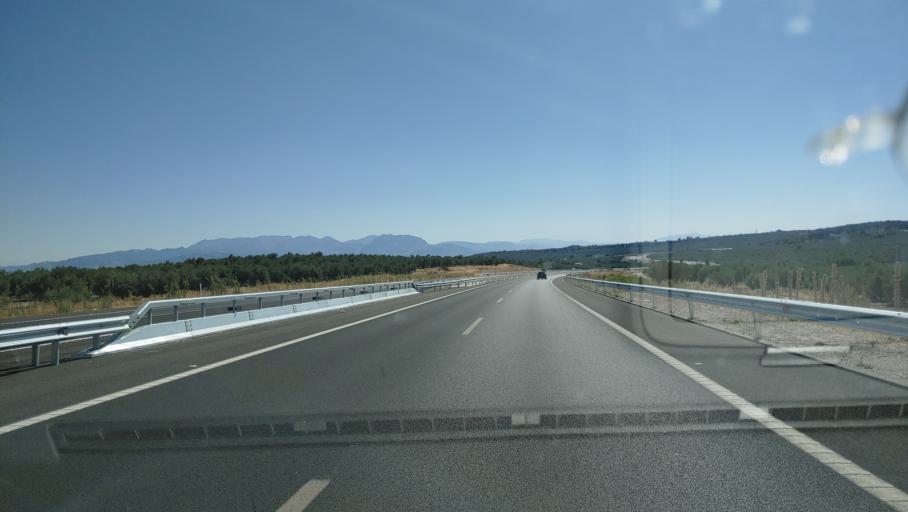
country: ES
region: Andalusia
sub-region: Provincia de Jaen
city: Sabiote
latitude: 38.0469
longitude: -3.3101
